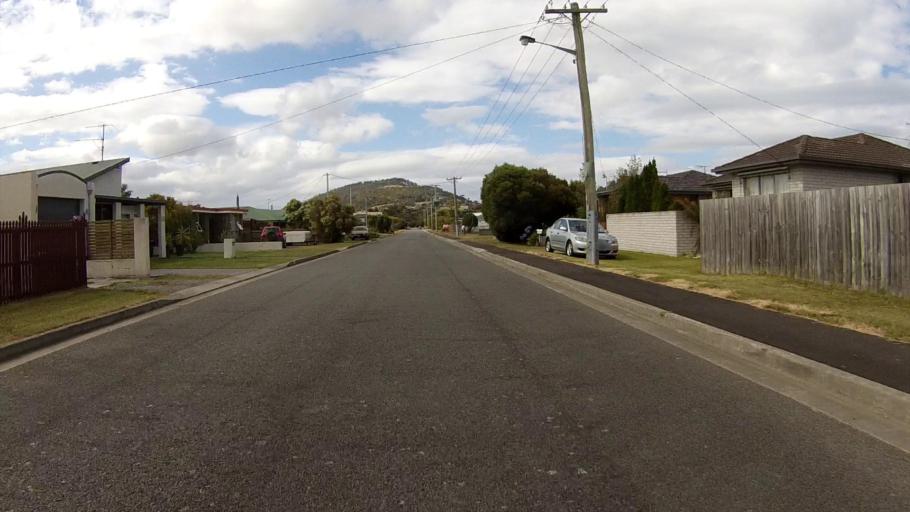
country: AU
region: Tasmania
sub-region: Clarence
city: Lauderdale
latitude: -42.8964
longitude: 147.4957
